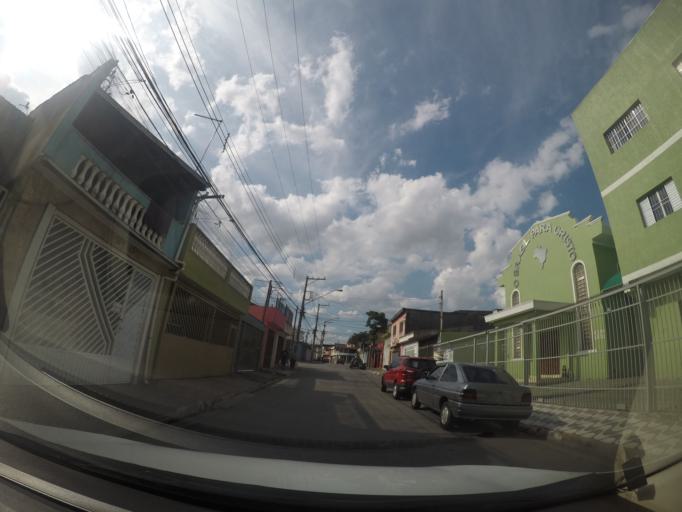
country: BR
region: Sao Paulo
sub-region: Guarulhos
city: Guarulhos
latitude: -23.4508
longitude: -46.5061
